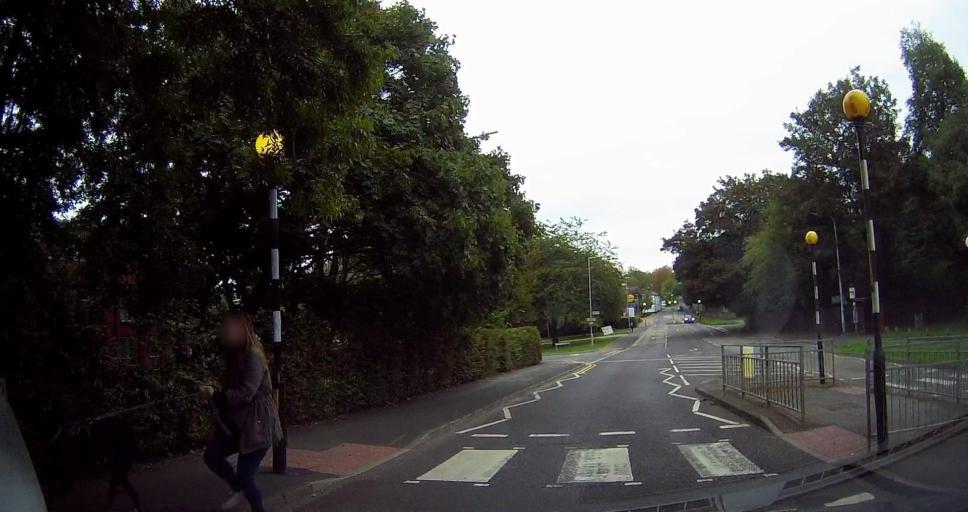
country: GB
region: England
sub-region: Kent
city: Sevenoaks
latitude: 51.2793
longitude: 0.1746
